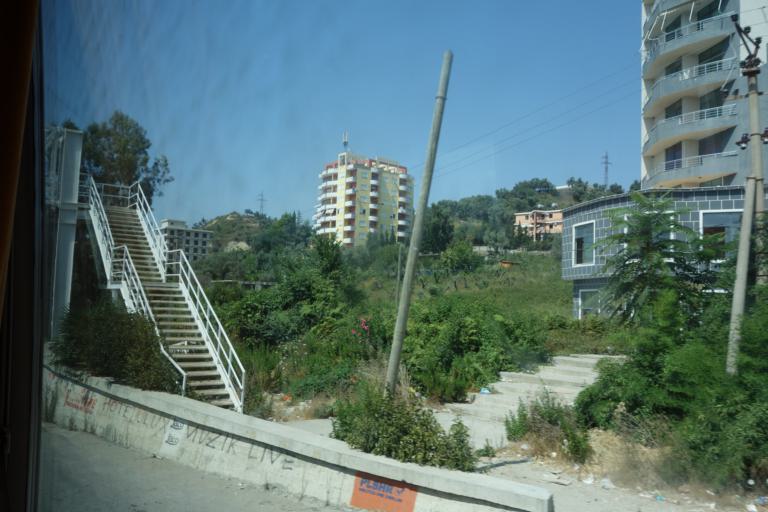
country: AL
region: Tirane
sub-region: Rrethi i Kavajes
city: Golem
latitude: 41.2677
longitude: 19.5216
